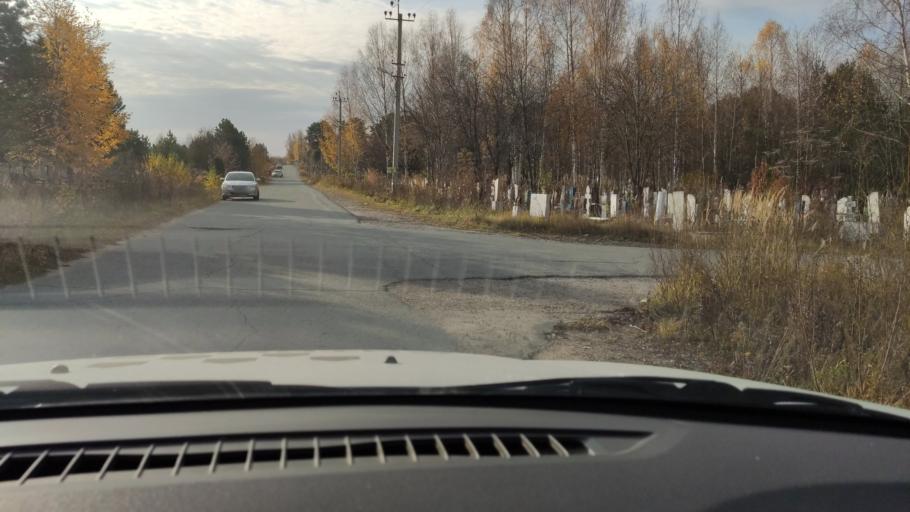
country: RU
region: Perm
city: Kondratovo
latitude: 58.0683
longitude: 56.1448
